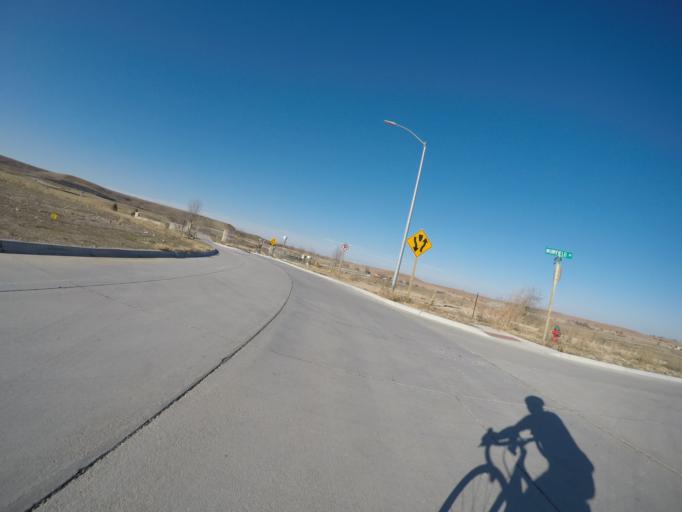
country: US
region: Kansas
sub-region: Riley County
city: Manhattan
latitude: 39.2195
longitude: -96.6413
